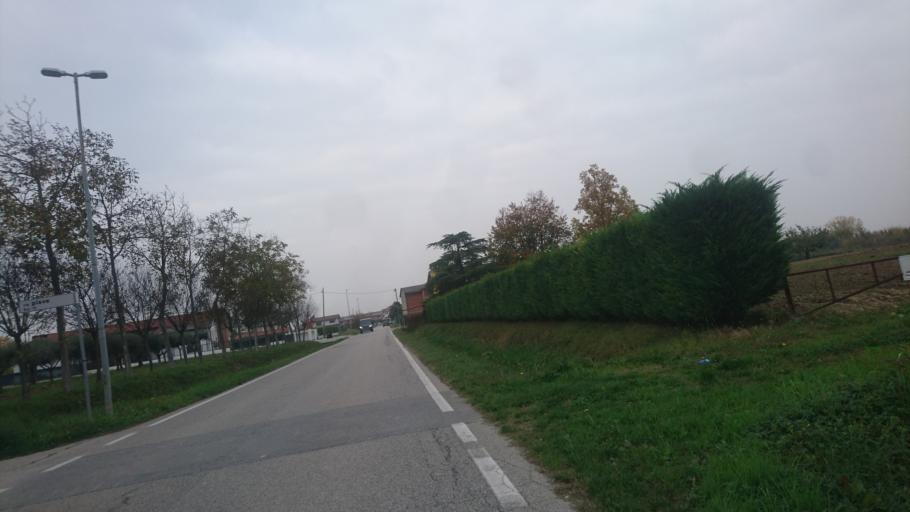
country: IT
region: Veneto
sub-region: Provincia di Venezia
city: Tombelle
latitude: 45.3910
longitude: 11.9789
